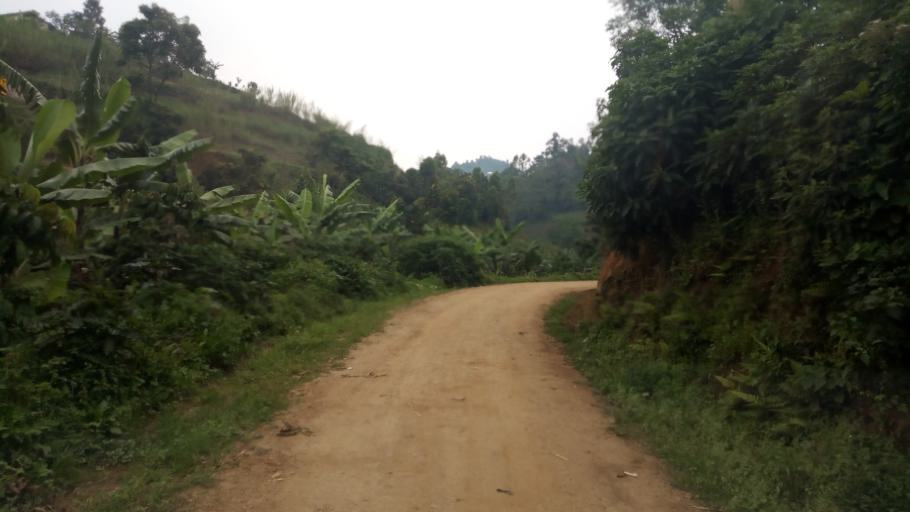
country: UG
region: Western Region
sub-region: Kisoro District
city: Kisoro
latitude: -1.2565
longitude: 29.6303
